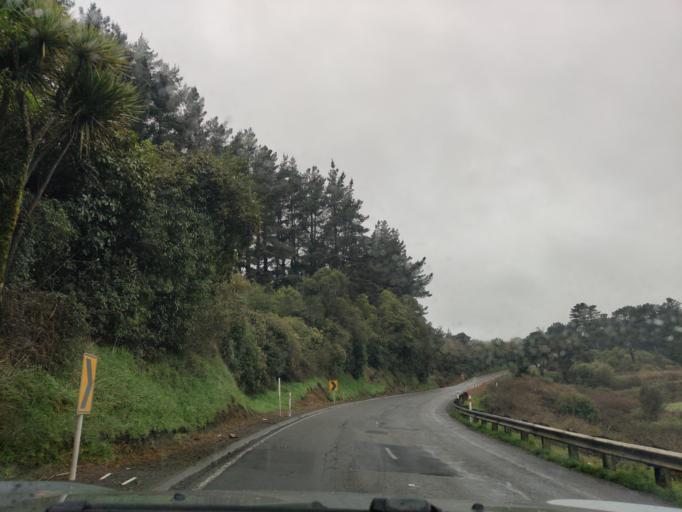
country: NZ
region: Manawatu-Wanganui
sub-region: Palmerston North City
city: Palmerston North
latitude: -40.0529
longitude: 176.2402
